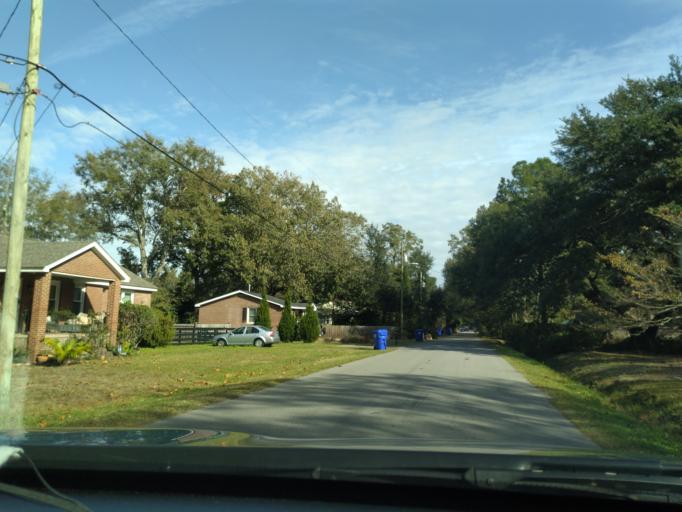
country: US
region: South Carolina
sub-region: Charleston County
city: North Charleston
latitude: 32.8021
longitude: -80.0145
